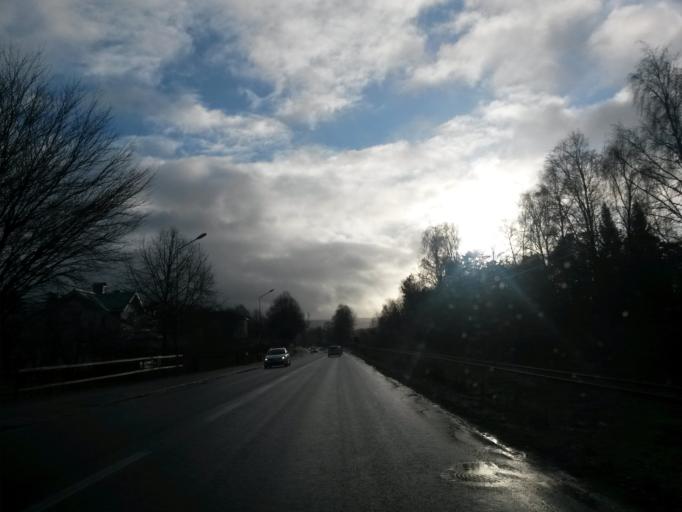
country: SE
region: Vaestra Goetaland
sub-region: Boras Kommun
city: Boras
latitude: 57.8214
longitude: 13.0076
